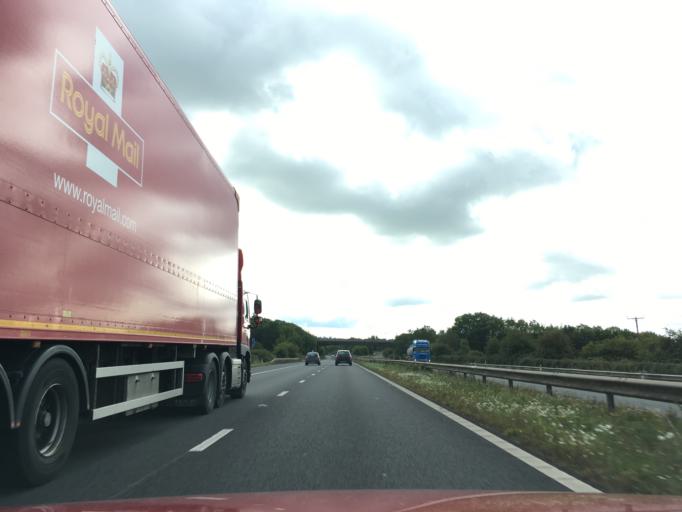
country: GB
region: England
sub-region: South Gloucestershire
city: Almondsbury
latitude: 51.5783
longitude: -2.5890
